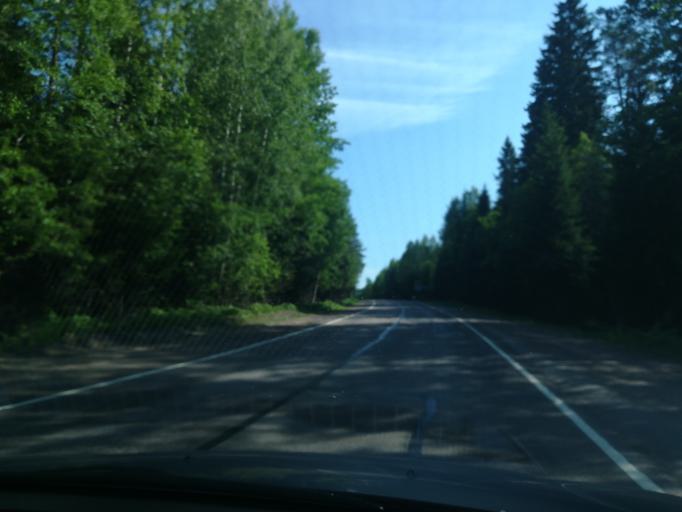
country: RU
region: Leningrad
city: Lesogorskiy
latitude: 60.9015
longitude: 28.8653
